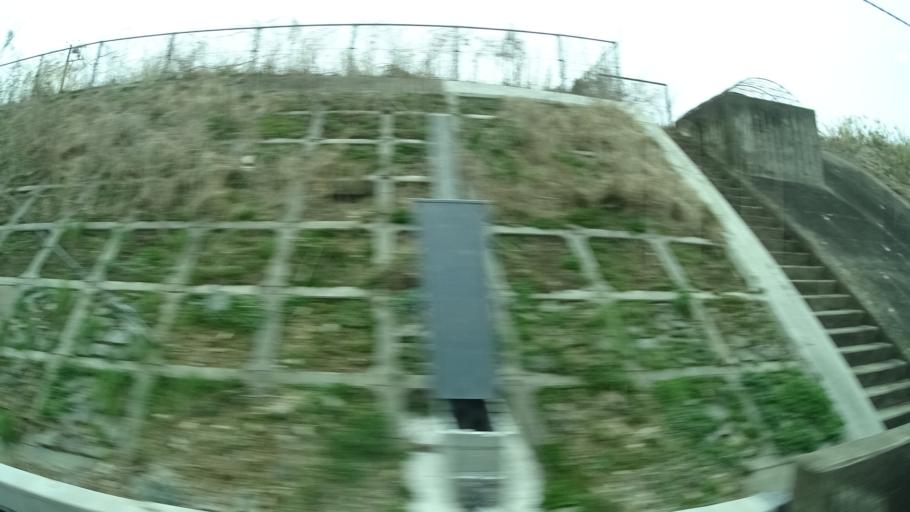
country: JP
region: Fukushima
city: Namie
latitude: 37.3616
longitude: 140.9925
